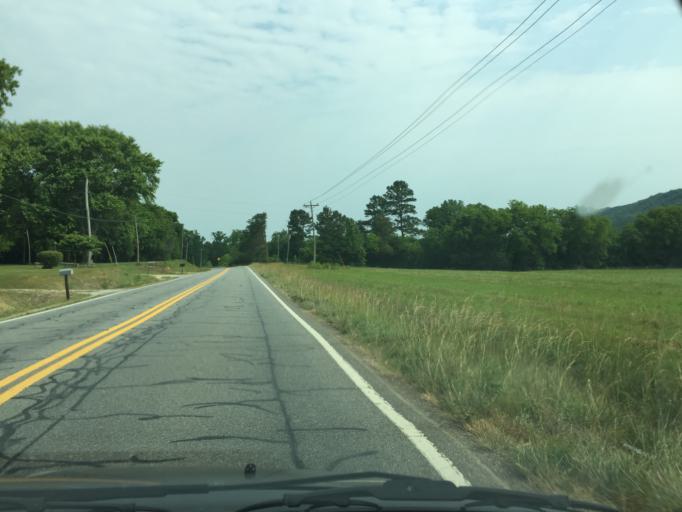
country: US
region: Georgia
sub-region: Catoosa County
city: Ringgold
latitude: 34.8401
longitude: -85.1400
